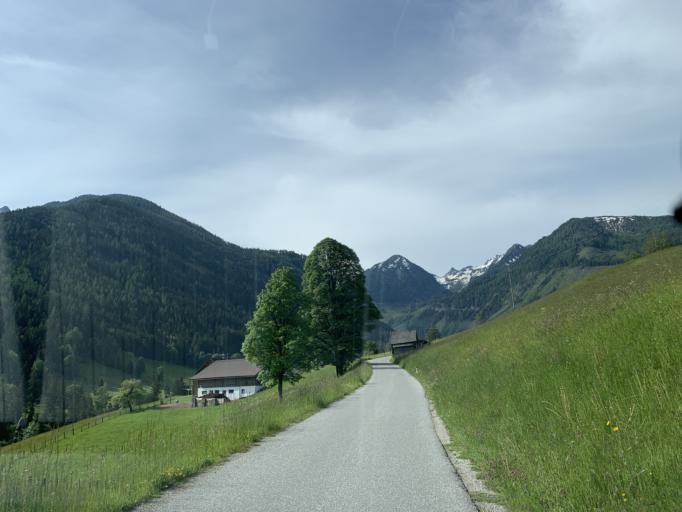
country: AT
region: Styria
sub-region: Politischer Bezirk Liezen
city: Schladming
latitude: 47.3683
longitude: 13.6664
